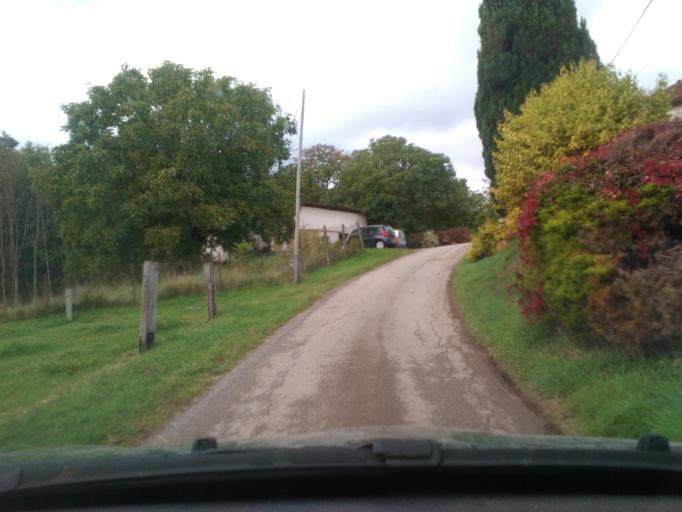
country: FR
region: Lorraine
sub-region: Departement des Vosges
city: Saint-Michel-sur-Meurthe
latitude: 48.3342
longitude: 6.8646
